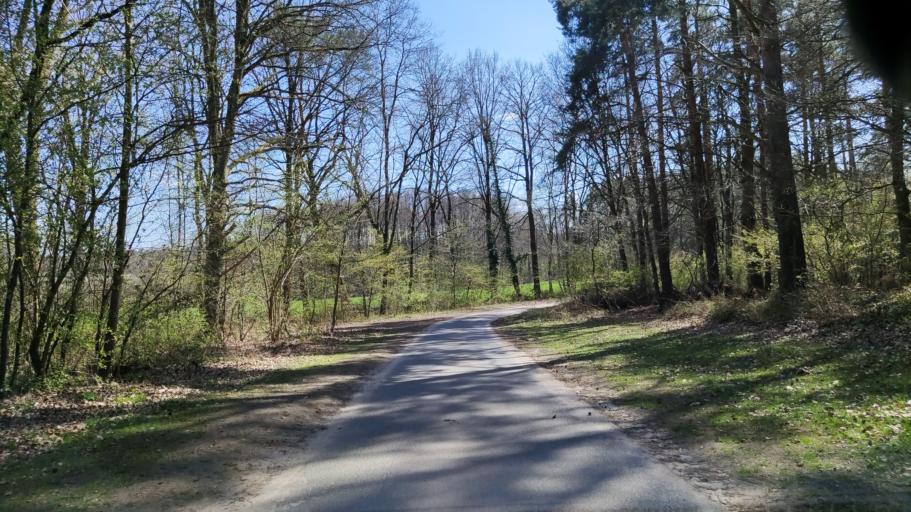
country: DE
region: Lower Saxony
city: Deutsch Evern
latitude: 53.1947
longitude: 10.4455
